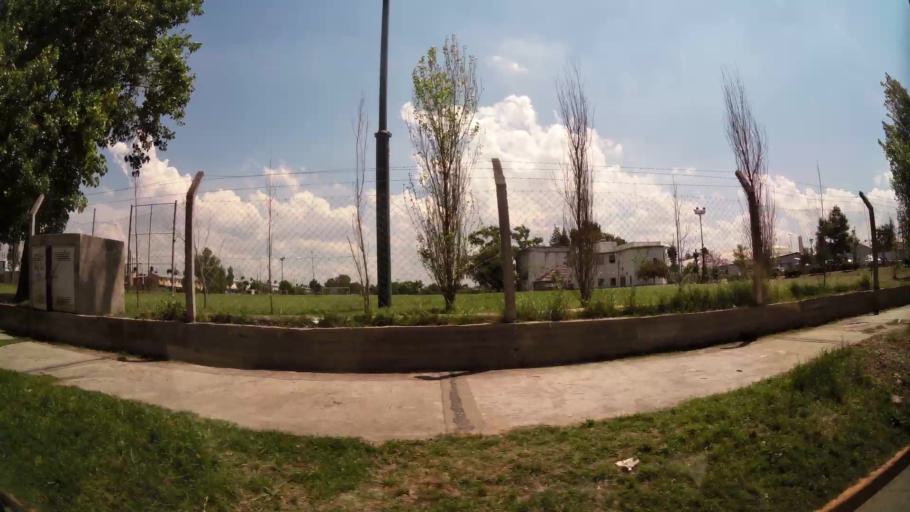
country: AR
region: Buenos Aires
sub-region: Partido de Tigre
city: Tigre
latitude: -34.4560
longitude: -58.5805
